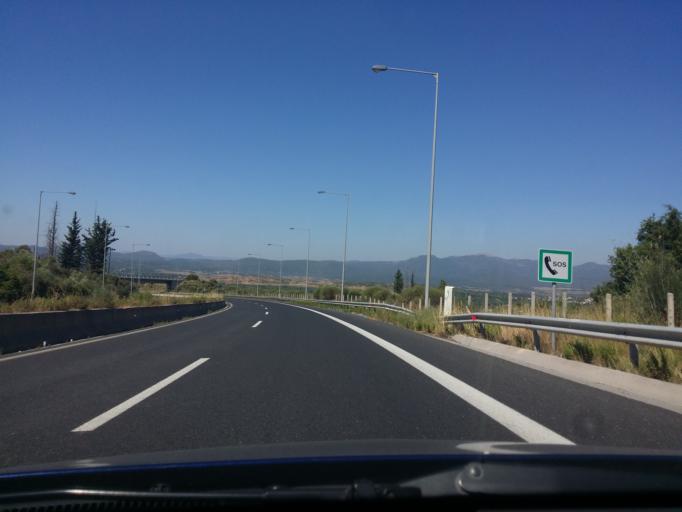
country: GR
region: Peloponnese
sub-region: Nomos Arkadias
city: Megalopoli
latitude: 37.3941
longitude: 22.1765
